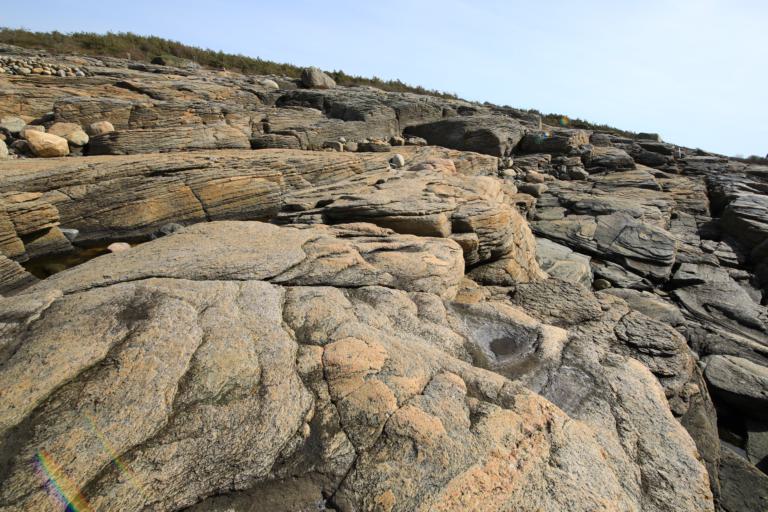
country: SE
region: Halland
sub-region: Kungsbacka Kommun
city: Frillesas
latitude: 57.2701
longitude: 12.1089
